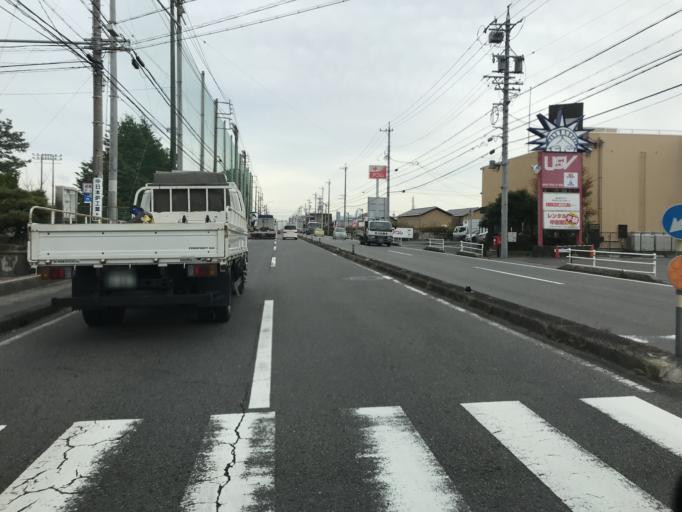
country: JP
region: Aichi
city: Kanie
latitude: 35.1846
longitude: 136.7978
